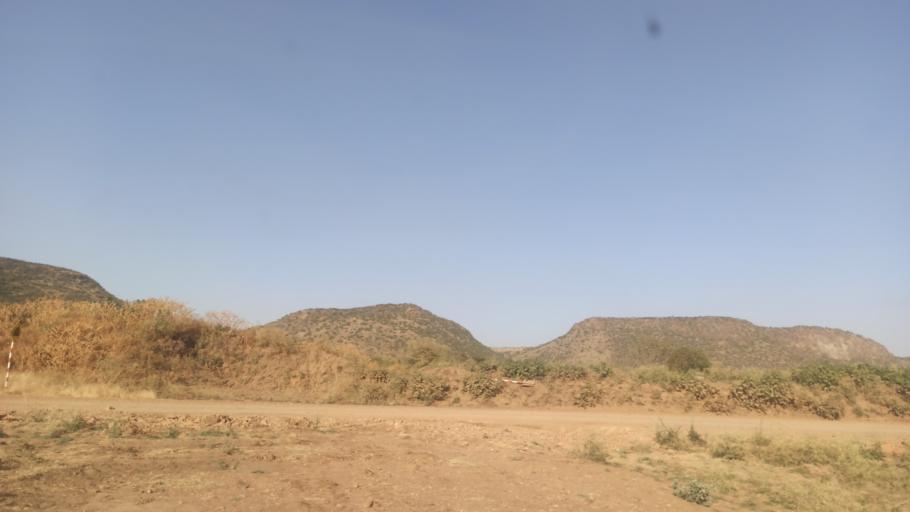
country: ET
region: Oromiya
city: Ziway
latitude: 7.9355
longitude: 38.6194
